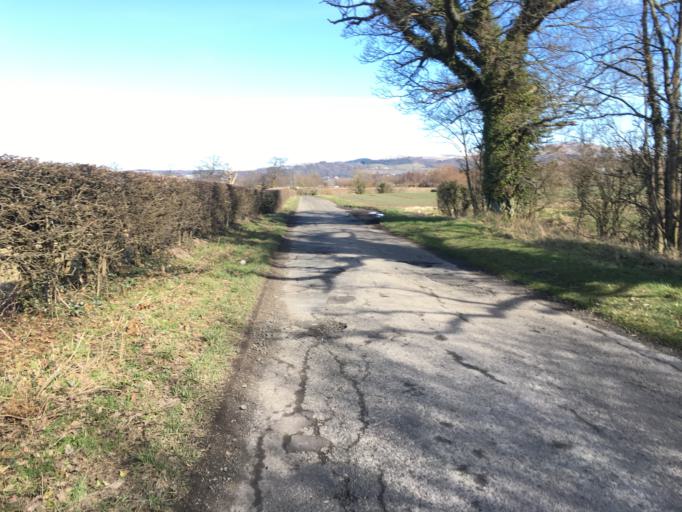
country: GB
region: Scotland
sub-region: Stirling
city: Bridge of Allan
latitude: 56.1338
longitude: -3.9834
